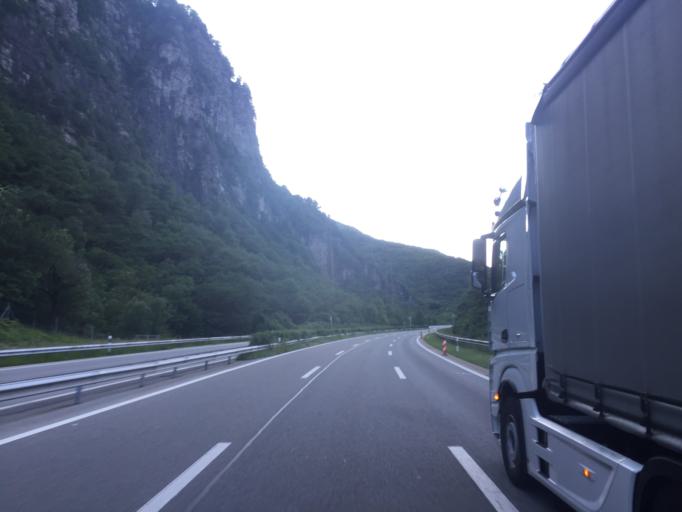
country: CH
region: Ticino
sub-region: Leventina District
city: Bodio
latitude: 46.4001
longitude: 8.8690
